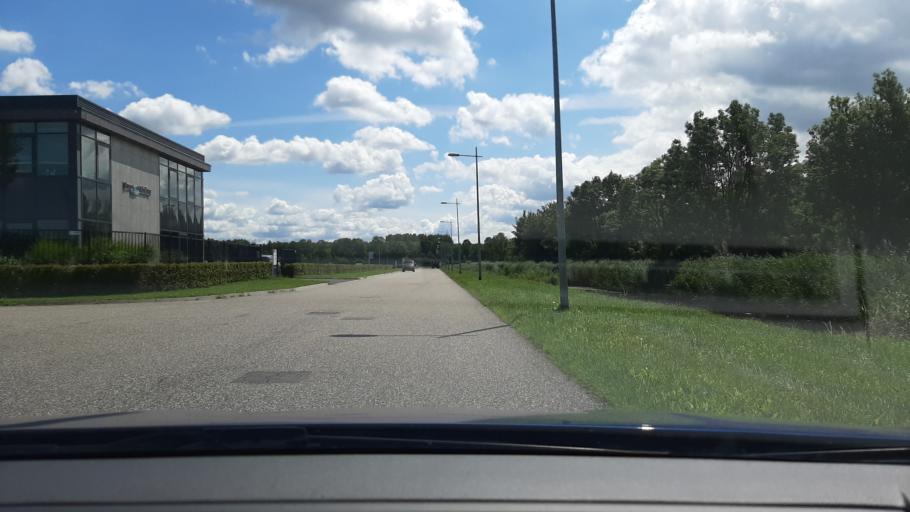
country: NL
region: Flevoland
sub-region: Gemeente Zeewolde
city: Zeewolde
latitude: 52.3486
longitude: 5.4906
